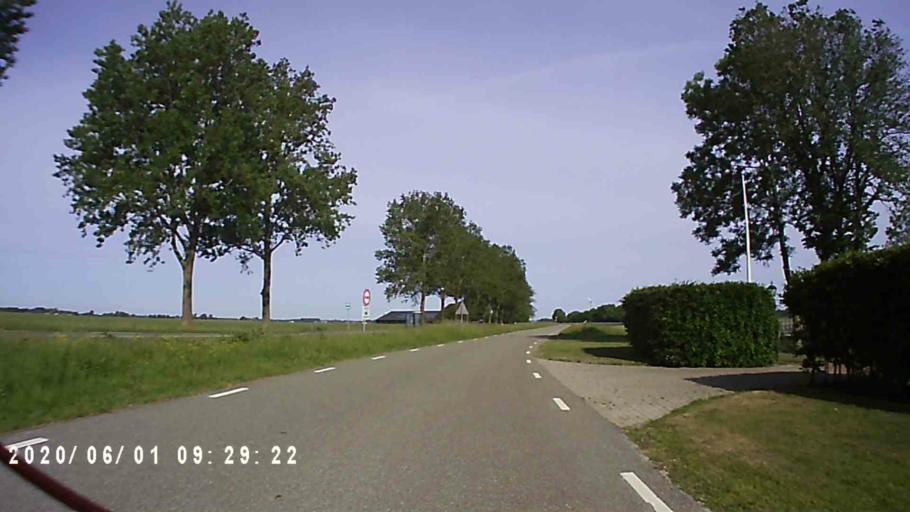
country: NL
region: Friesland
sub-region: Gemeente Leeuwarderadeel
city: Stiens
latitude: 53.2651
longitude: 5.7357
